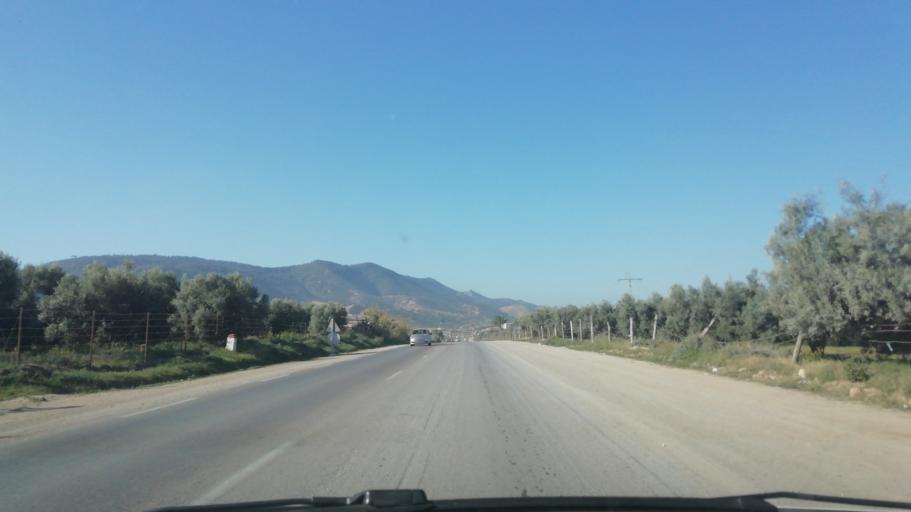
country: DZ
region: Mascara
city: Sig
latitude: 35.5340
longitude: -0.1426
